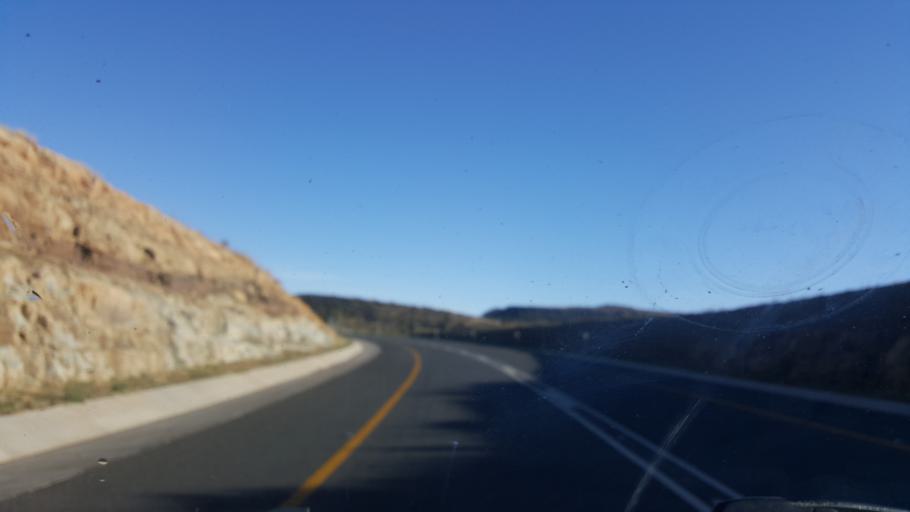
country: ZA
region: Eastern Cape
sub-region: Chris Hani District Municipality
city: Middelburg
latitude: -31.3778
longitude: 25.0341
